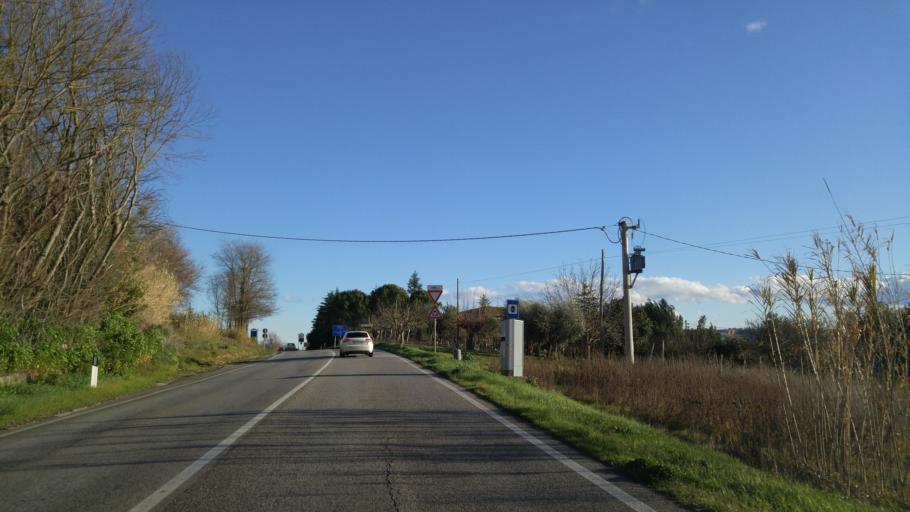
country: IT
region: The Marches
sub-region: Provincia di Ancona
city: Camerano
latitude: 43.5080
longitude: 13.5448
